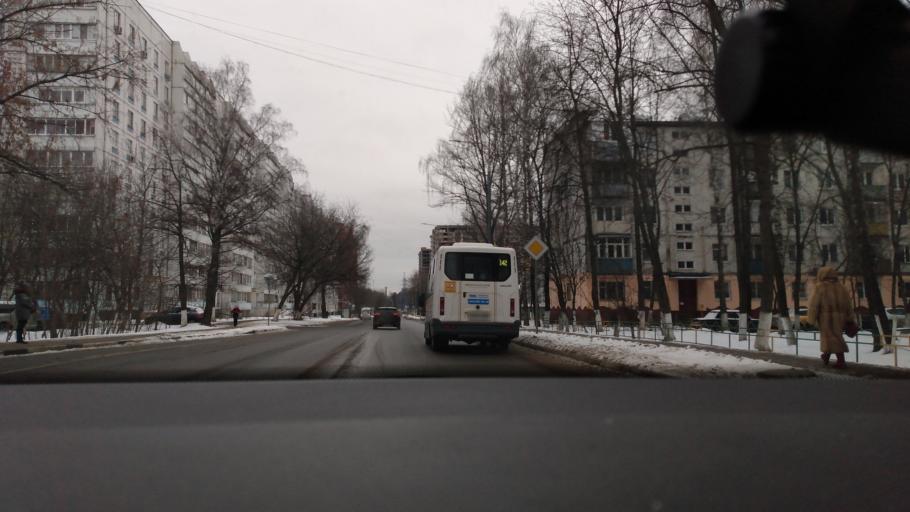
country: RU
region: Moskovskaya
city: Zheleznodorozhnyy
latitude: 55.7434
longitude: 38.0293
